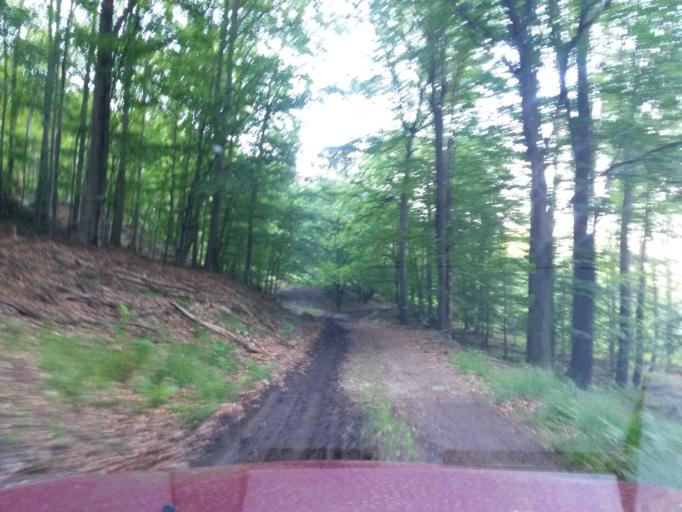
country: SK
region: Kosicky
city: Moldava nad Bodvou
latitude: 48.7311
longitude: 21.0619
